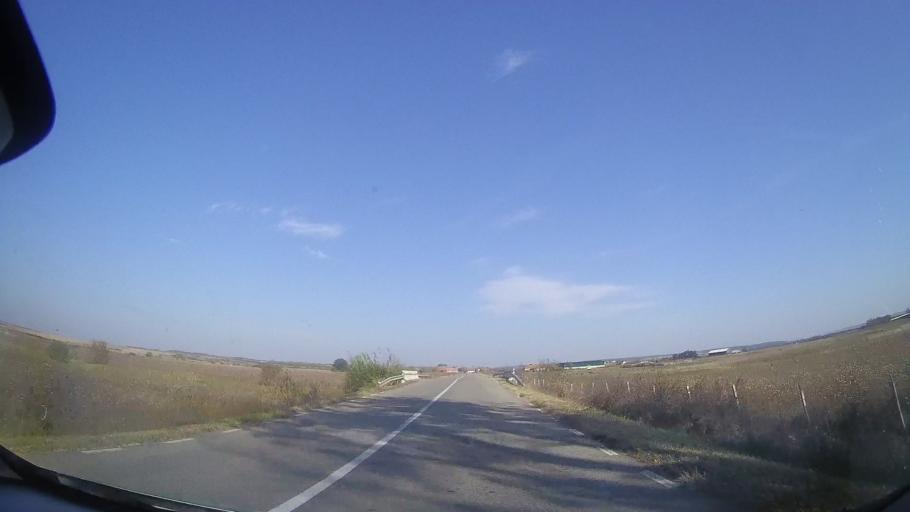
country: RO
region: Timis
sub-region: Comuna Ghizela
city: Ghizela
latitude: 45.7856
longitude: 21.7311
